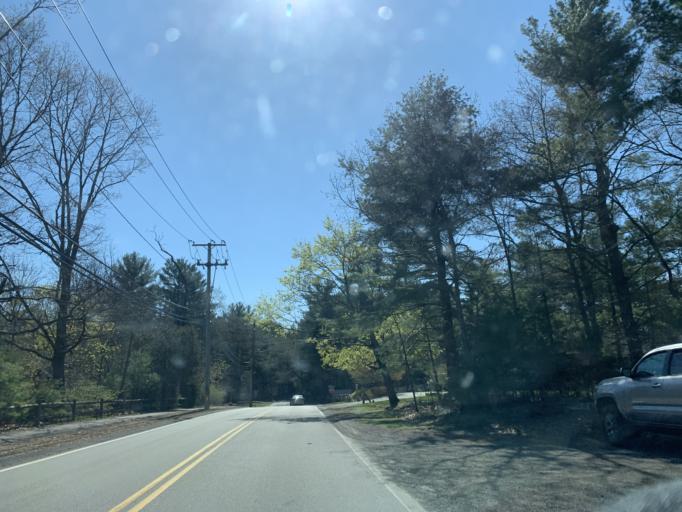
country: US
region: Massachusetts
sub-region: Norfolk County
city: Walpole
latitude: 42.1534
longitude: -71.2165
